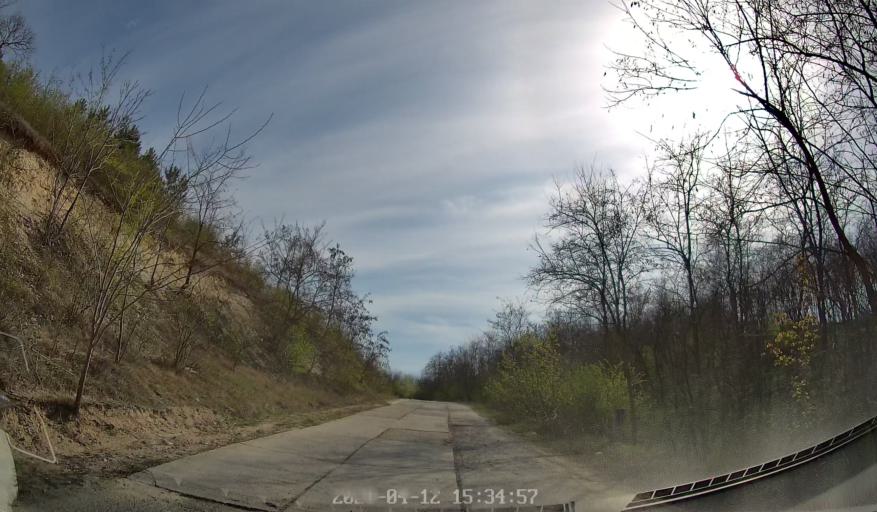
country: MD
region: Telenesti
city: Cocieri
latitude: 47.3267
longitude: 29.0712
